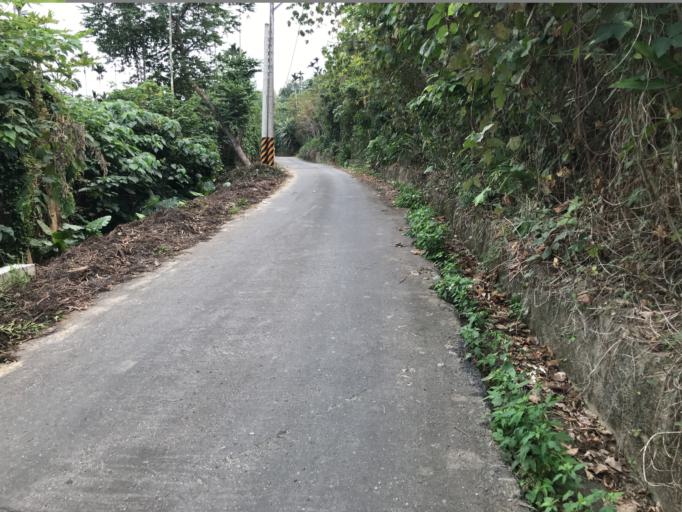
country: TW
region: Taiwan
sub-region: Chiayi
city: Jiayi Shi
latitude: 23.4264
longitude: 120.5266
